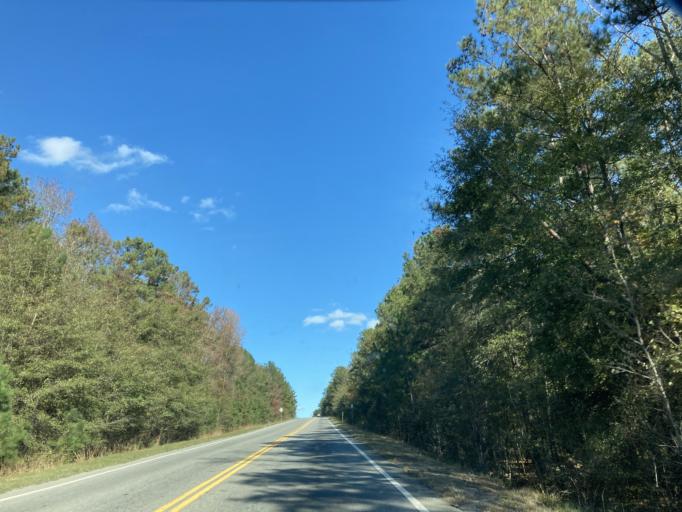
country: US
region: Georgia
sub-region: Jones County
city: Gray
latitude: 32.8982
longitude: -83.5281
